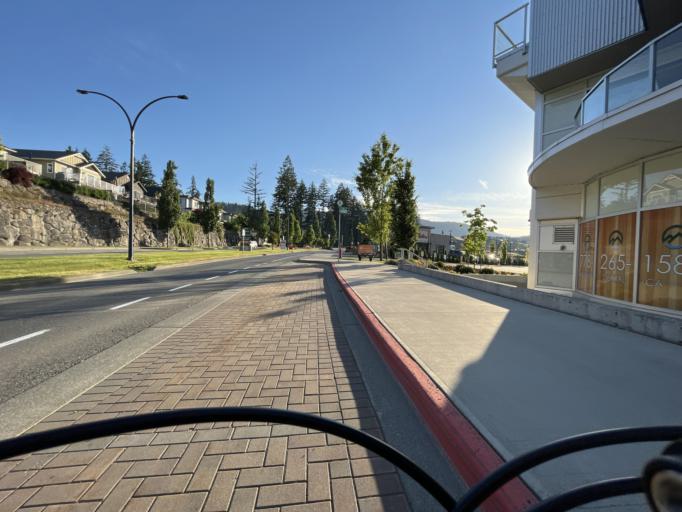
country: CA
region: British Columbia
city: Langford
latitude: 48.4452
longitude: -123.5339
